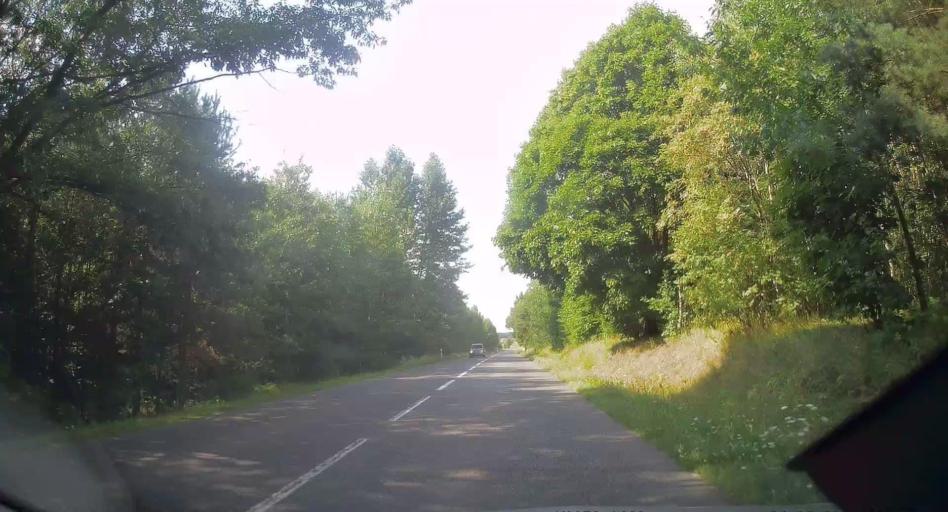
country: PL
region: Swietokrzyskie
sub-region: Powiat kielecki
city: Lopuszno
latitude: 50.9268
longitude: 20.2393
